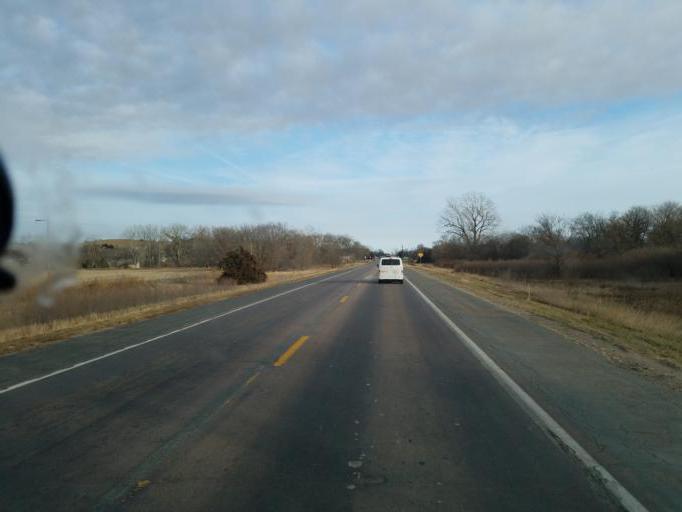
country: US
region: South Dakota
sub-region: Union County
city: Dakota Dunes
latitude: 42.4480
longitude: -96.5795
